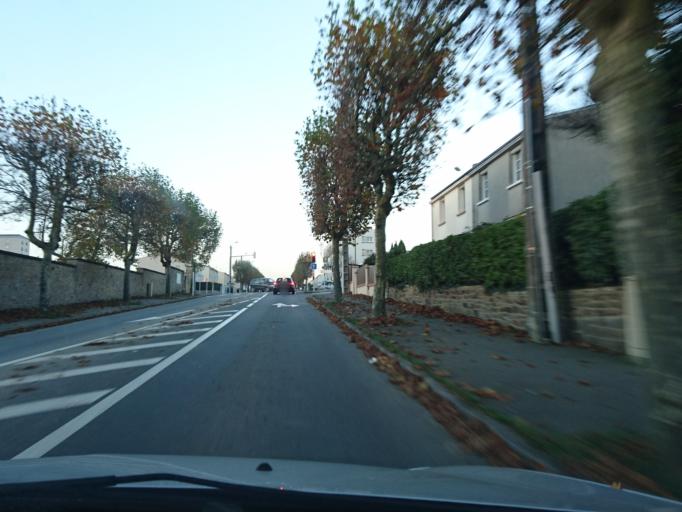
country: FR
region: Brittany
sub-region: Departement du Finistere
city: Brest
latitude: 48.4146
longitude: -4.4867
